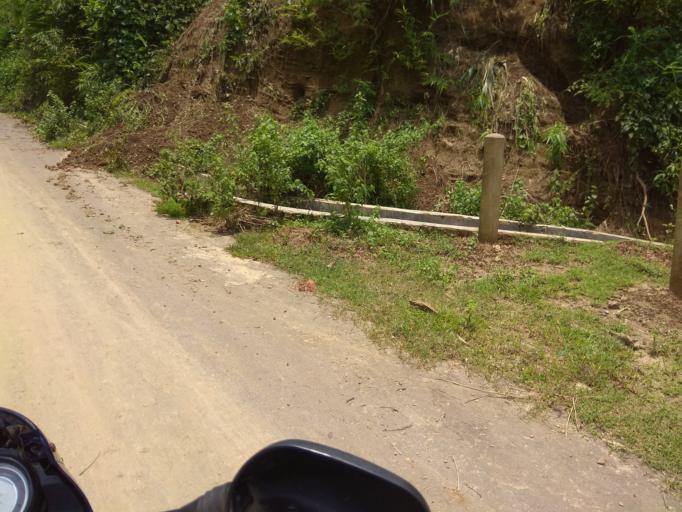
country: BD
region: Chittagong
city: Manikchari
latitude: 22.8942
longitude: 91.9222
